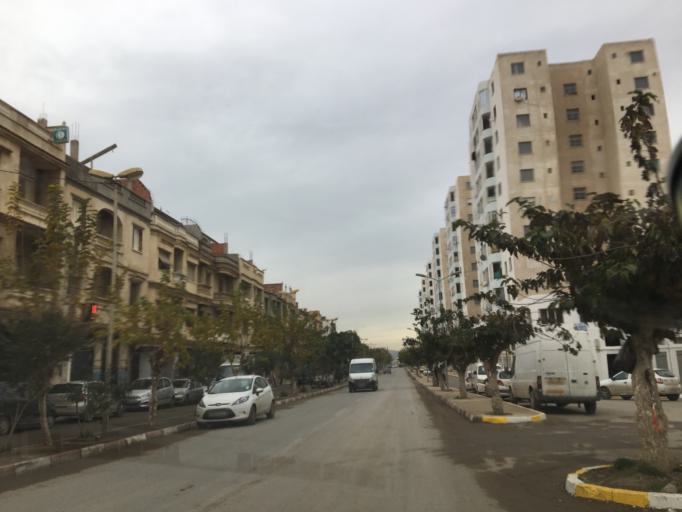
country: DZ
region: Alger
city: Ain Taya
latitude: 36.7913
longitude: 3.2426
